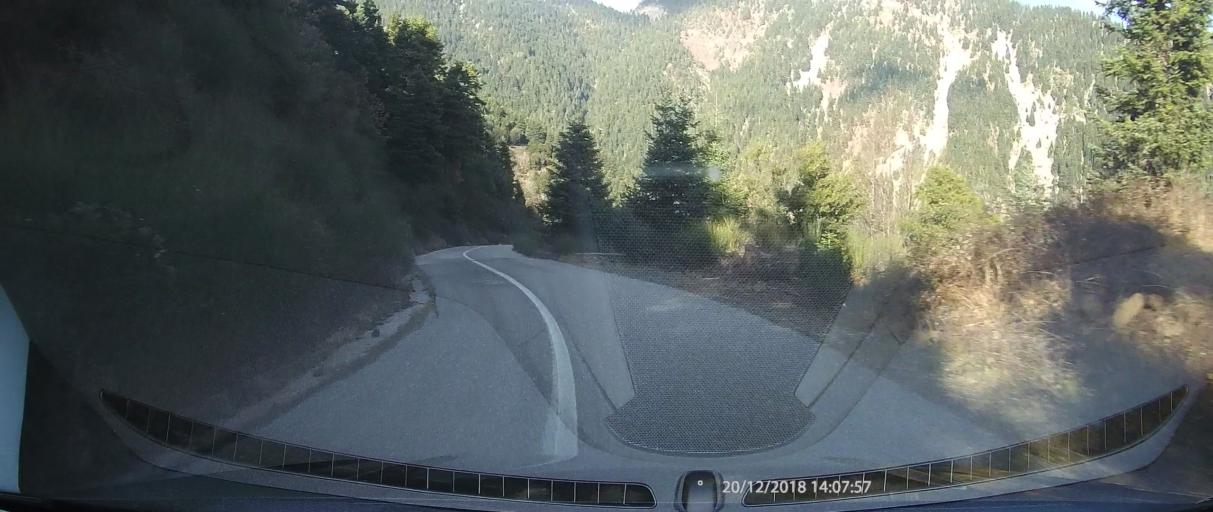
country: GR
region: West Greece
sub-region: Nomos Aitolias kai Akarnanias
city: Thermo
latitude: 38.7528
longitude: 21.6468
